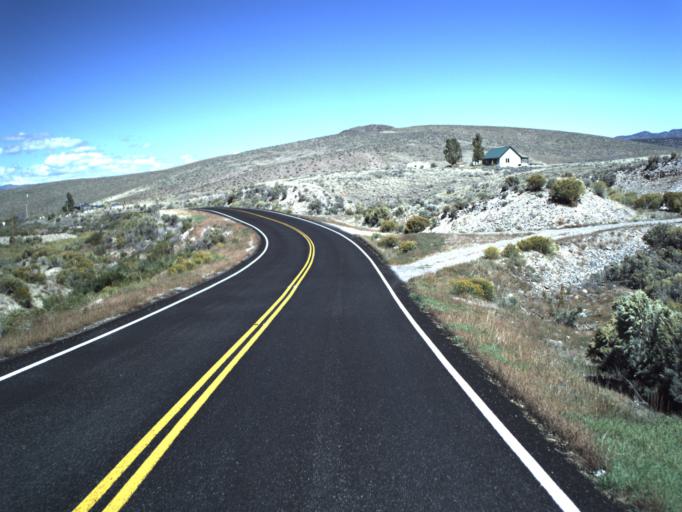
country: US
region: Utah
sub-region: Piute County
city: Junction
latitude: 38.0989
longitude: -111.9839
